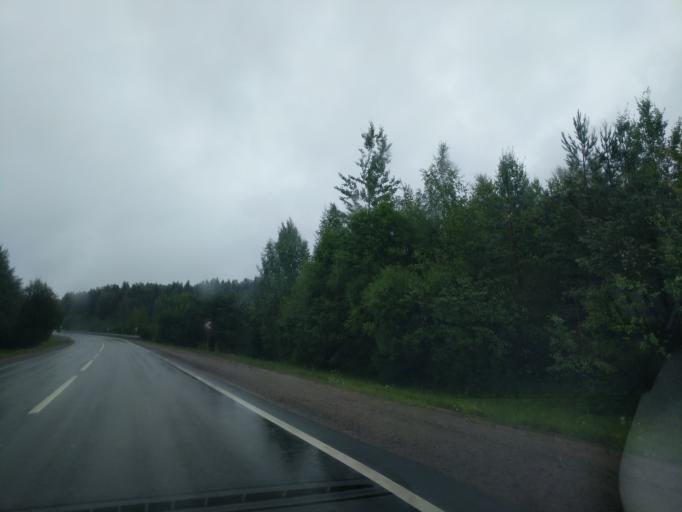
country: BY
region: Minsk
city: Bal'shavik
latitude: 54.1101
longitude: 27.5299
